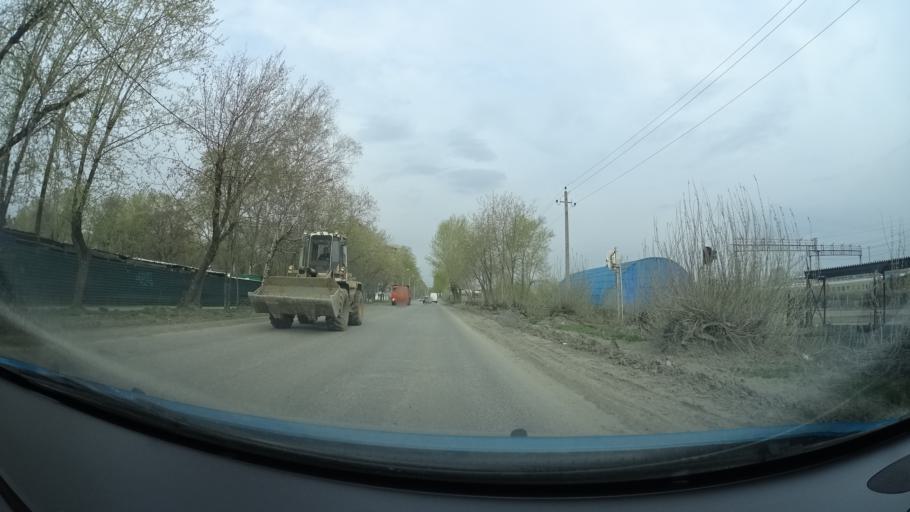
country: RU
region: Perm
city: Kondratovo
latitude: 58.0022
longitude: 56.1757
